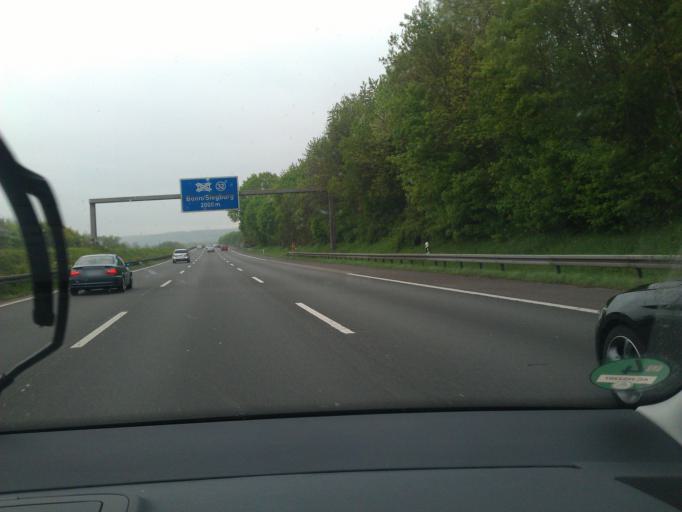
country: DE
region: North Rhine-Westphalia
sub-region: Regierungsbezirk Koln
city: Siegburg
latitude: 50.7967
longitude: 7.2303
